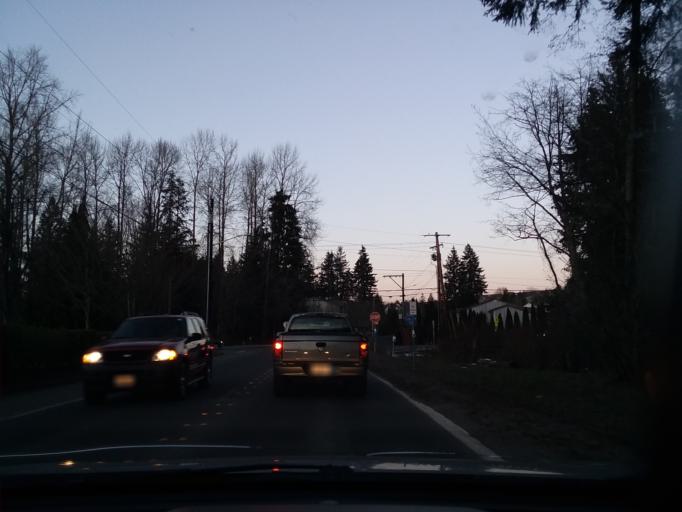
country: US
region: Washington
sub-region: Snohomish County
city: Martha Lake
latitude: 47.8808
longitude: -122.2577
